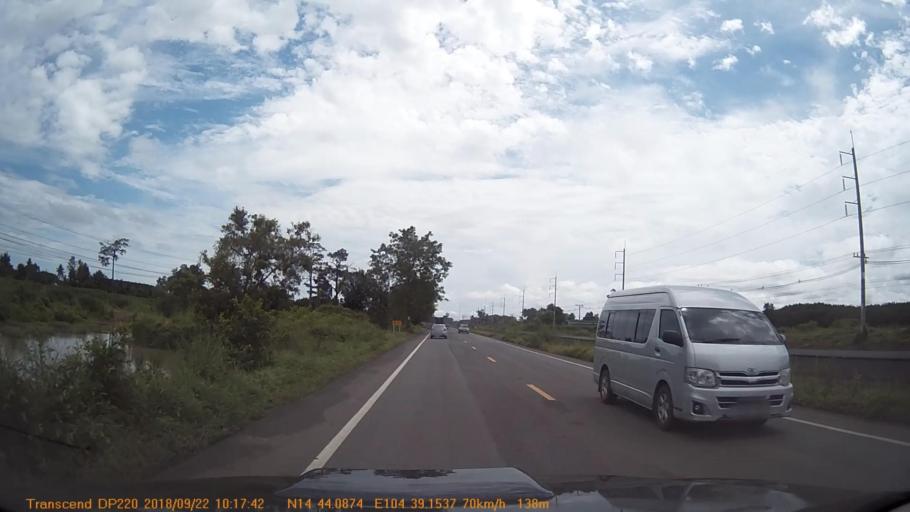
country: TH
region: Sisaket
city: Benchalak
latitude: 14.7348
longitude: 104.6526
